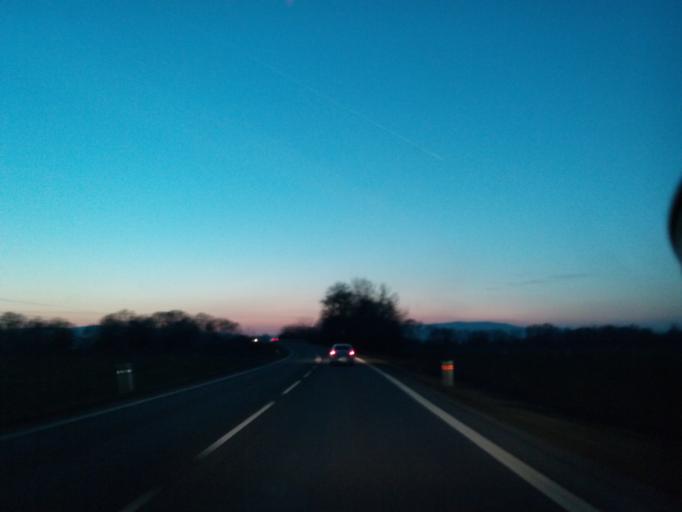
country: SK
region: Kosicky
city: Trebisov
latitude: 48.7013
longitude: 21.7817
